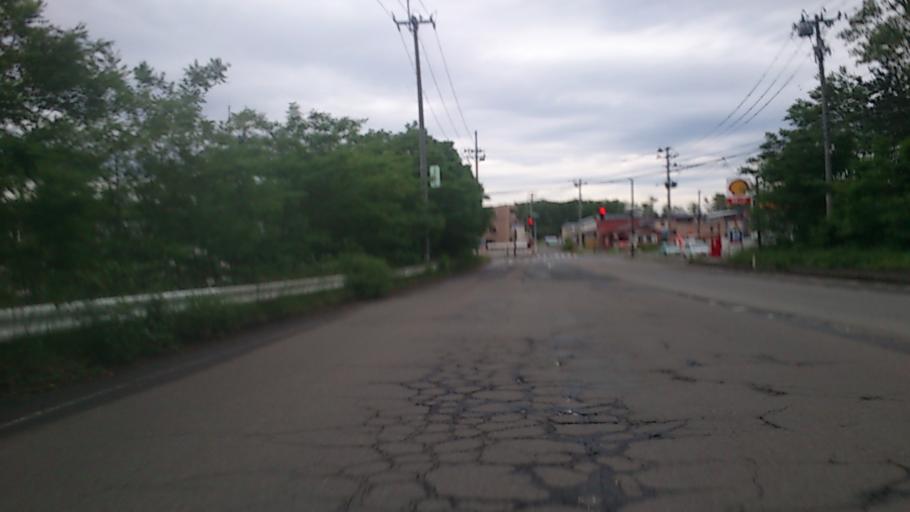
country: JP
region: Akita
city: Noshiromachi
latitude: 40.1879
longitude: 140.0114
